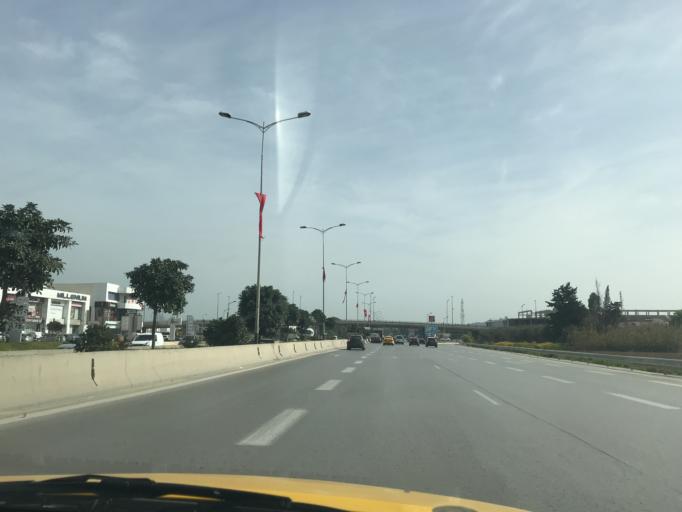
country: TN
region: Tunis
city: Al Marsa
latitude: 36.8691
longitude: 10.3101
